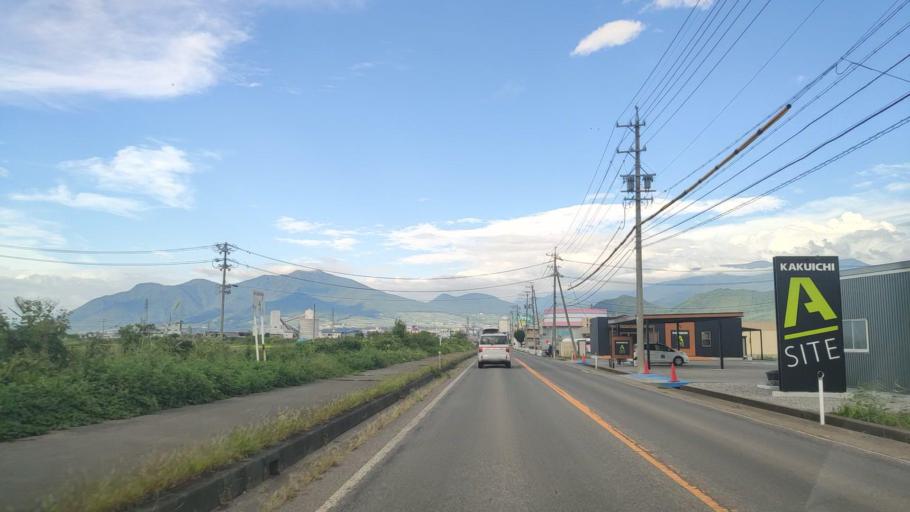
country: JP
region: Nagano
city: Nakano
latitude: 36.7277
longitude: 138.3381
